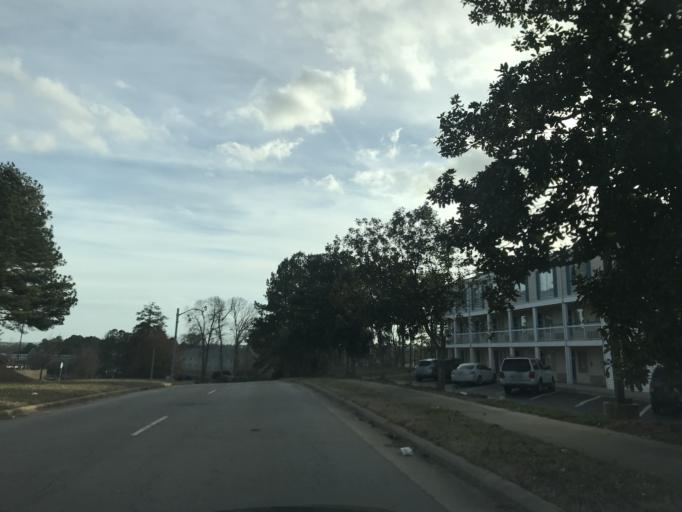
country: US
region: North Carolina
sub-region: Wake County
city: Raleigh
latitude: 35.8142
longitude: -78.6023
